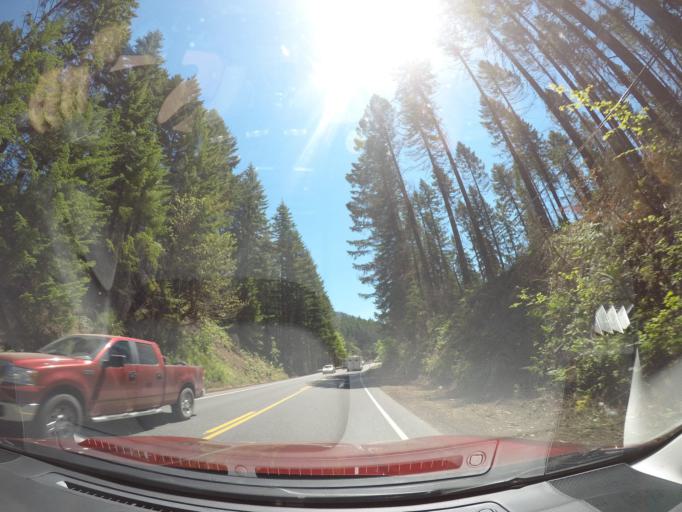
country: US
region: Oregon
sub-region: Linn County
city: Mill City
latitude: 44.7282
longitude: -122.1390
